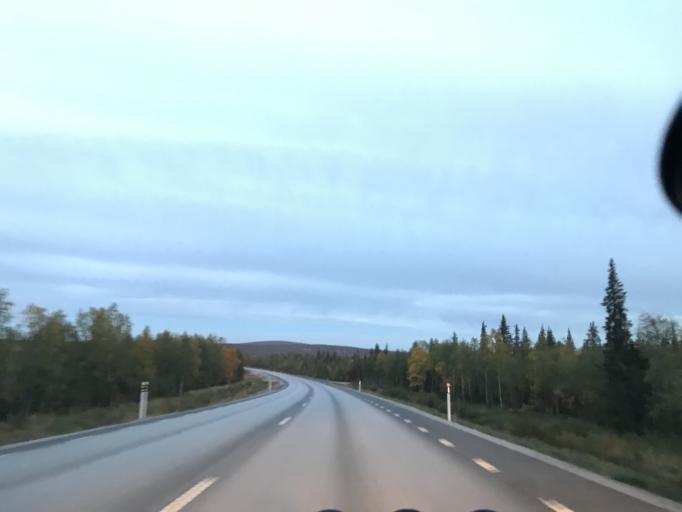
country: SE
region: Norrbotten
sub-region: Gallivare Kommun
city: Malmberget
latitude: 67.6478
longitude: 21.0258
